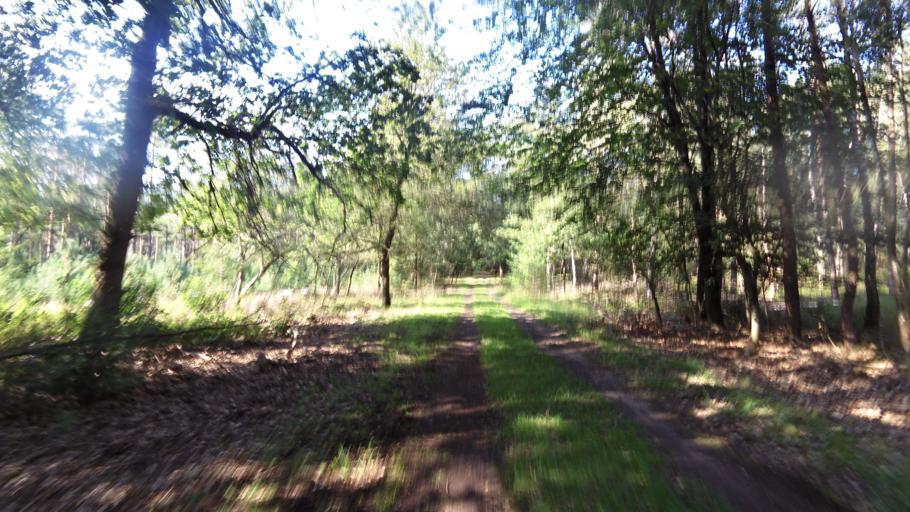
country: NL
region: Gelderland
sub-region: Gemeente Apeldoorn
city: Beekbergen
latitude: 52.1215
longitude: 5.9426
